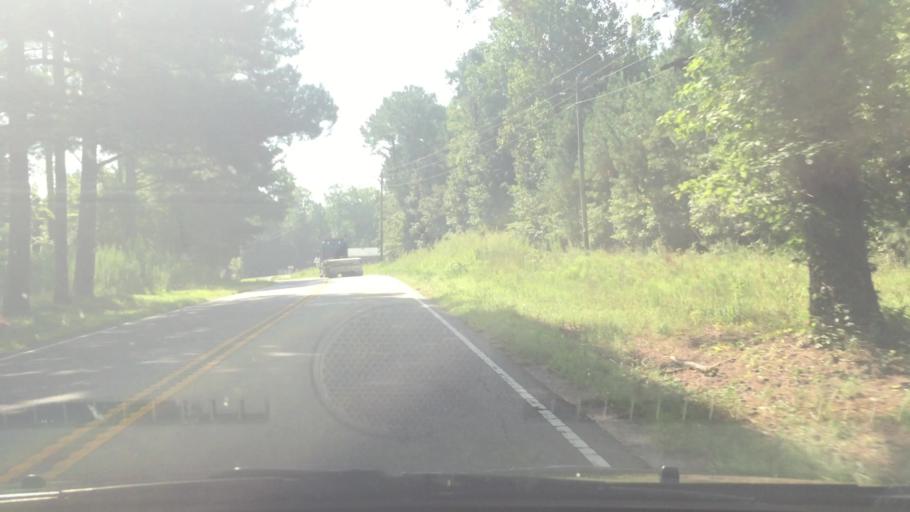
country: US
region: Virginia
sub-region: Sussex County
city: Sussex
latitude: 37.0149
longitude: -77.2802
